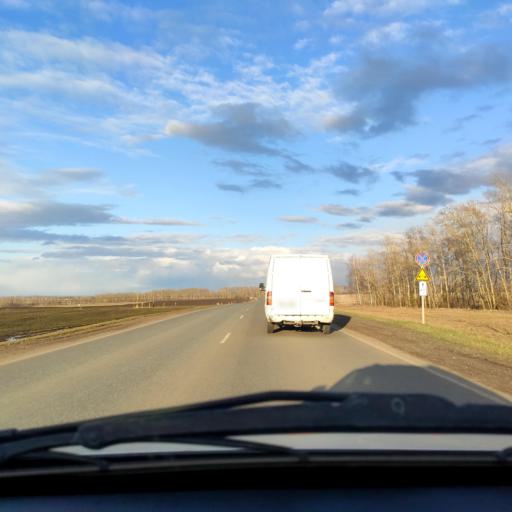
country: RU
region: Bashkortostan
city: Avdon
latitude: 54.5805
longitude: 55.7664
